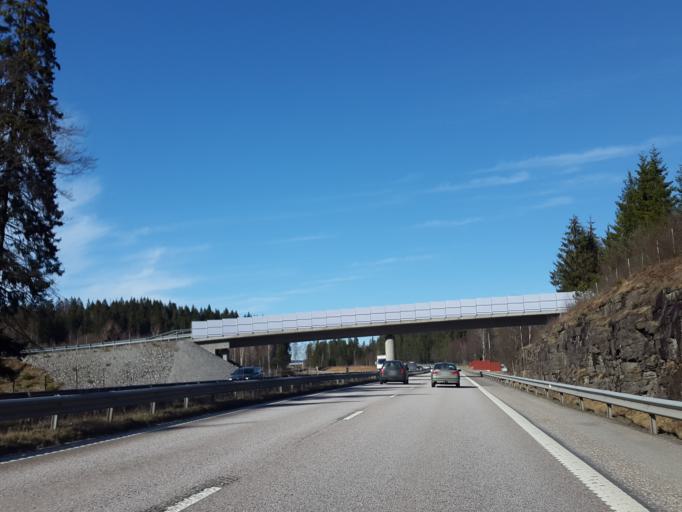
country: SE
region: Vaestra Goetaland
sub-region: Alingsas Kommun
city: Ingared
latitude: 57.8754
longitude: 12.4930
